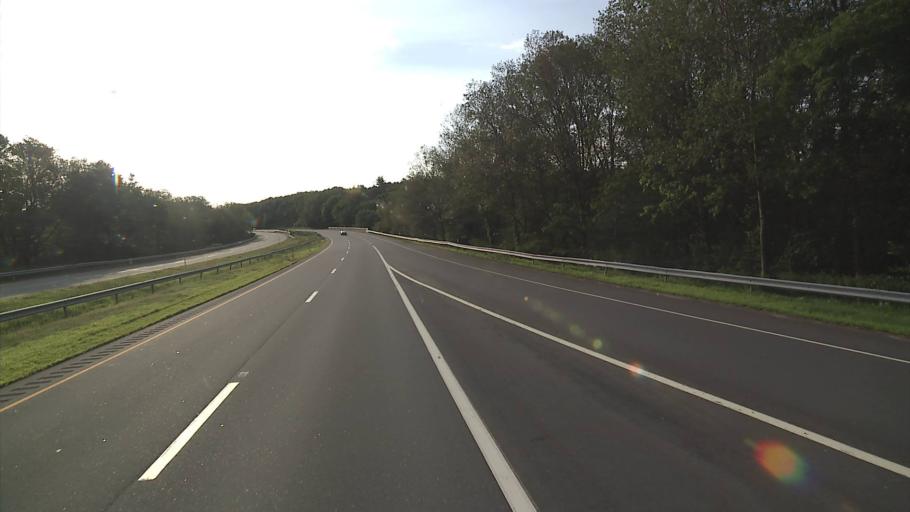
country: US
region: Connecticut
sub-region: New London County
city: Montville Center
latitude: 41.5610
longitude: -72.1608
